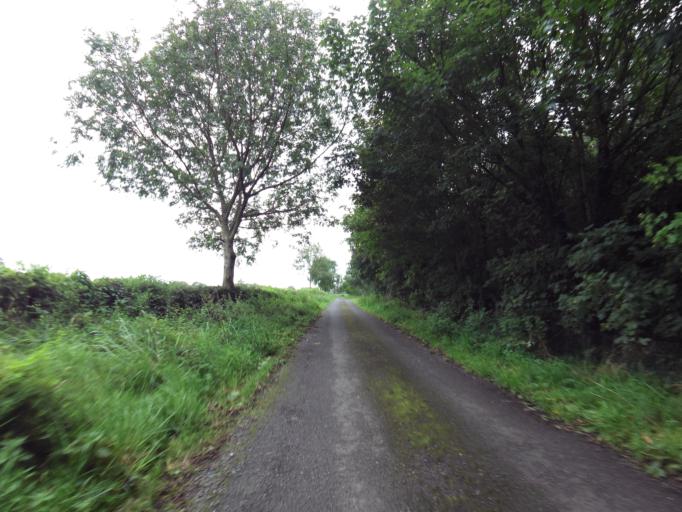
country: IE
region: Leinster
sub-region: Uibh Fhaili
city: Ferbane
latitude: 53.2383
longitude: -7.7370
